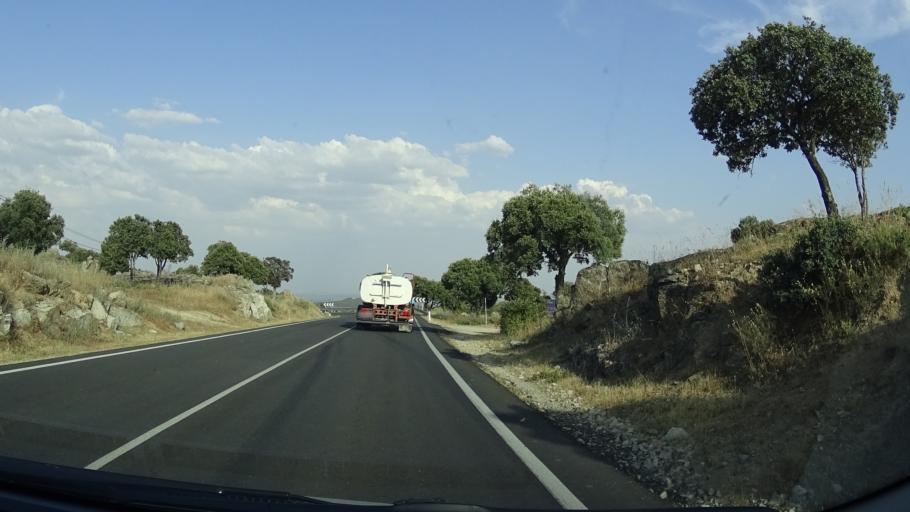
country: ES
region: Madrid
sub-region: Provincia de Madrid
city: Hoyo de Manzanares
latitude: 40.6215
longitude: -3.8919
